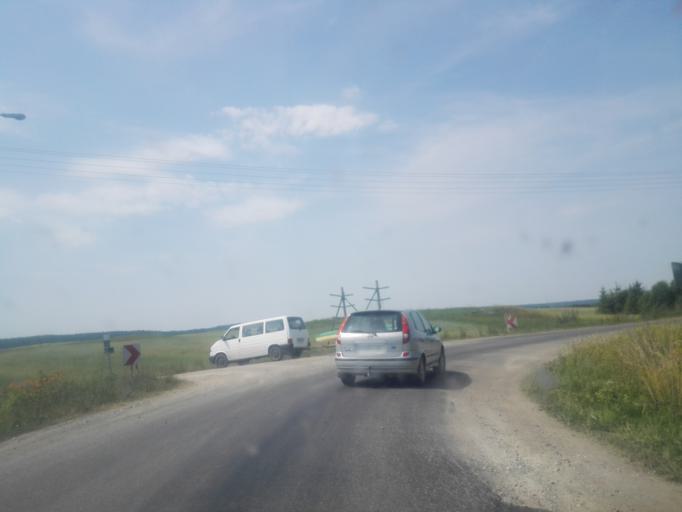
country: PL
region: Podlasie
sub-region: Powiat sejnenski
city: Krasnopol
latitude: 54.0527
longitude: 23.1372
